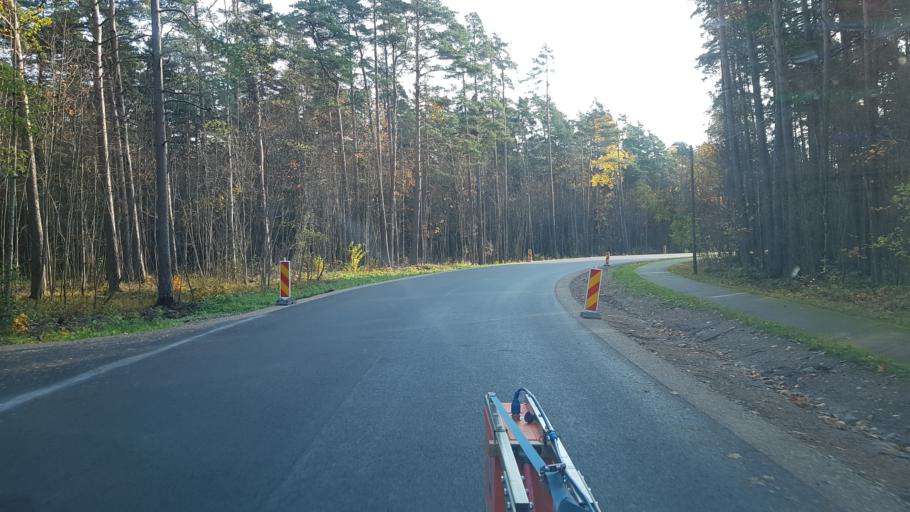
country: EE
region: Paernumaa
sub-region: Paikuse vald
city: Paikuse
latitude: 58.3667
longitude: 24.5999
